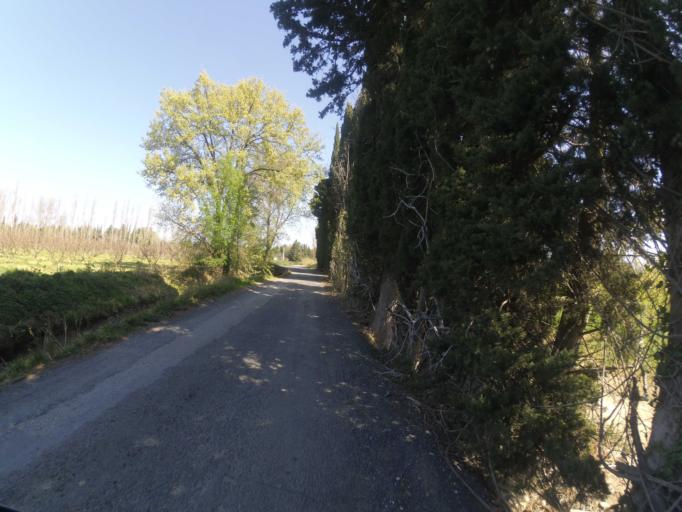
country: FR
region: Languedoc-Roussillon
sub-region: Departement des Pyrenees-Orientales
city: Pezilla-la-Riviere
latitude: 42.6666
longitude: 2.7597
